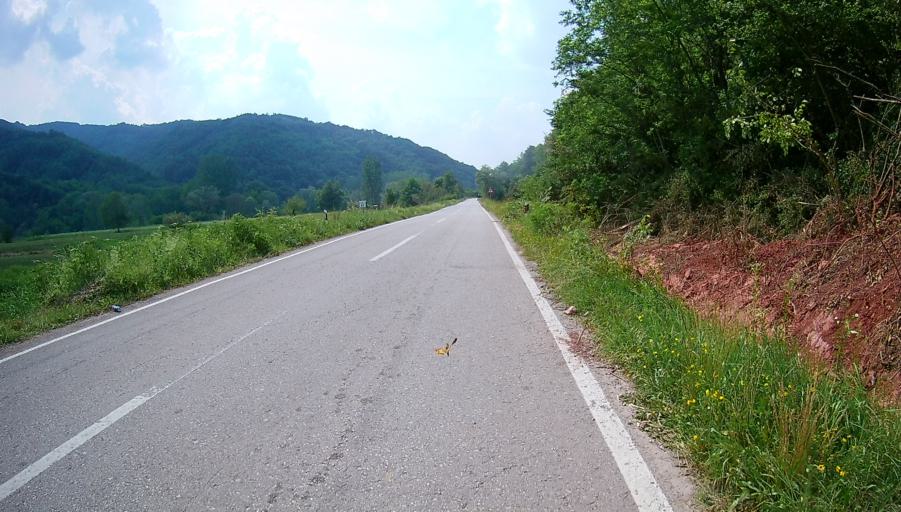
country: RS
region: Central Serbia
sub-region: Nisavski Okrug
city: Gadzin Han
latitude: 43.1655
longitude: 22.0940
